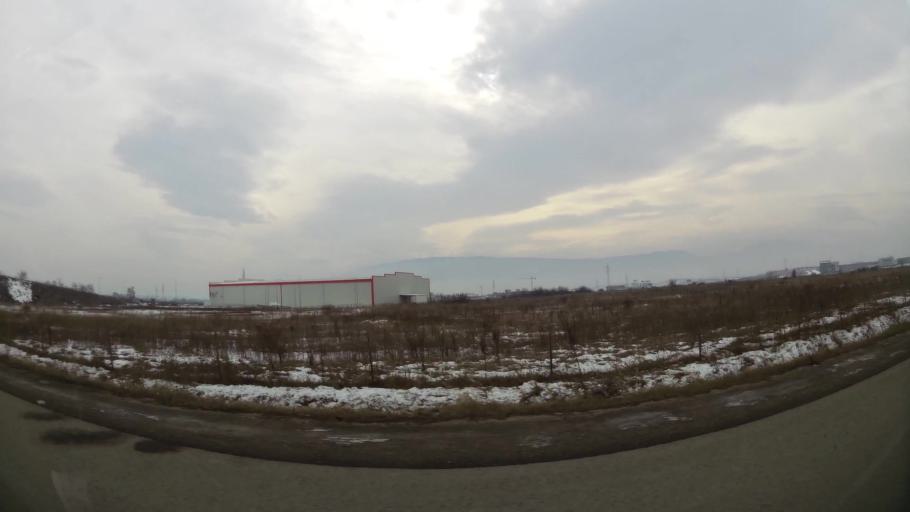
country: MK
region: Suto Orizari
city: Suto Orizare
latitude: 42.0529
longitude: 21.3899
